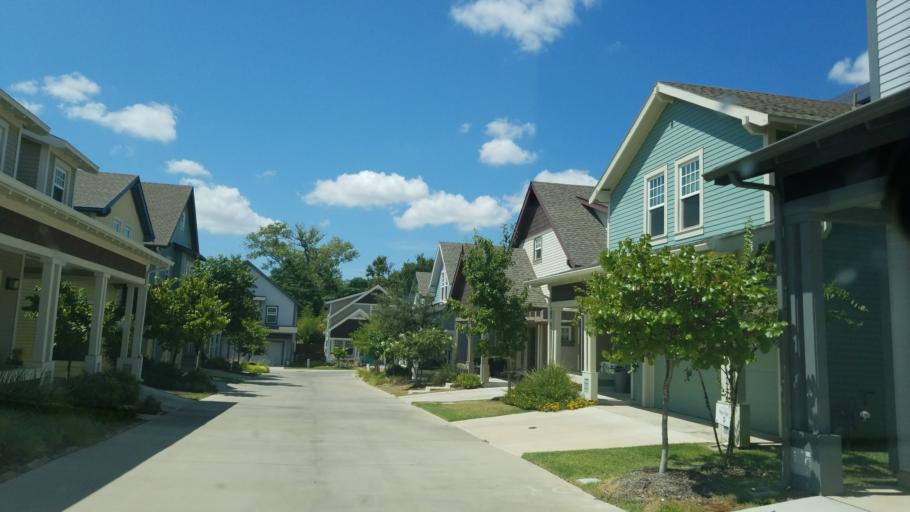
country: US
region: Texas
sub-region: Dallas County
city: Dallas
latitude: 32.7534
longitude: -96.8320
